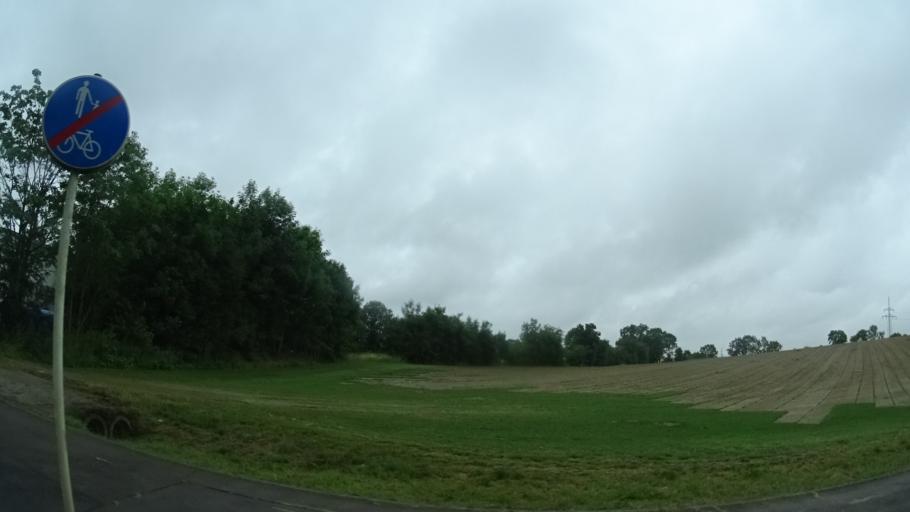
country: LU
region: Luxembourg
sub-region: Canton d'Esch-sur-Alzette
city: Sanem
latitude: 49.5427
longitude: 5.9332
